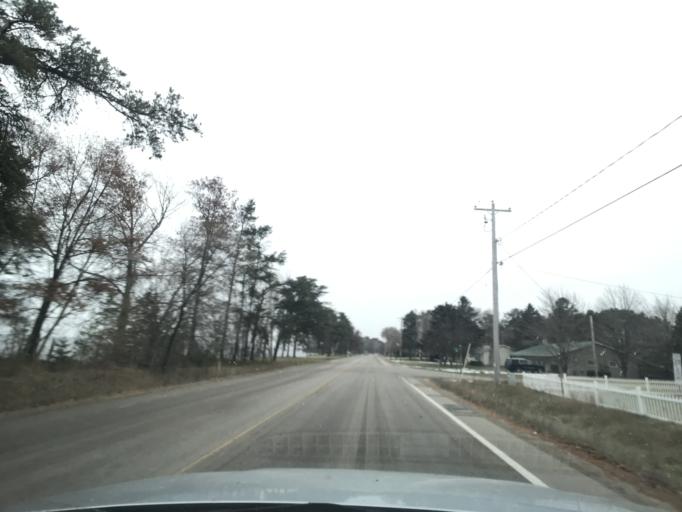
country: US
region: Wisconsin
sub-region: Marinette County
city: Marinette
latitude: 45.0486
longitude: -87.6253
